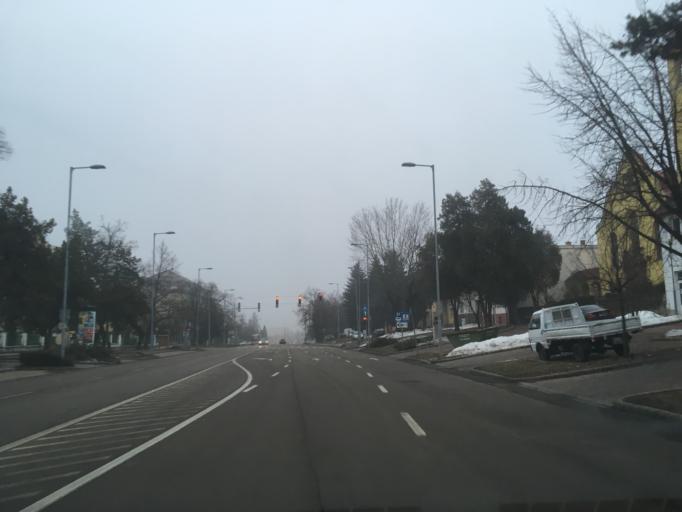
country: HU
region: Heves
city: Eger
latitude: 47.8938
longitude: 20.3768
